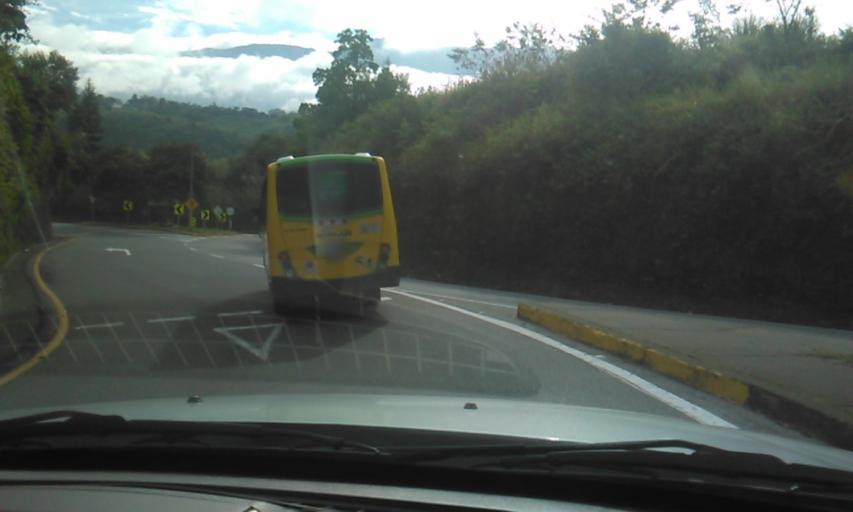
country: CO
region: Quindio
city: Armenia
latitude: 4.4870
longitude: -75.7041
